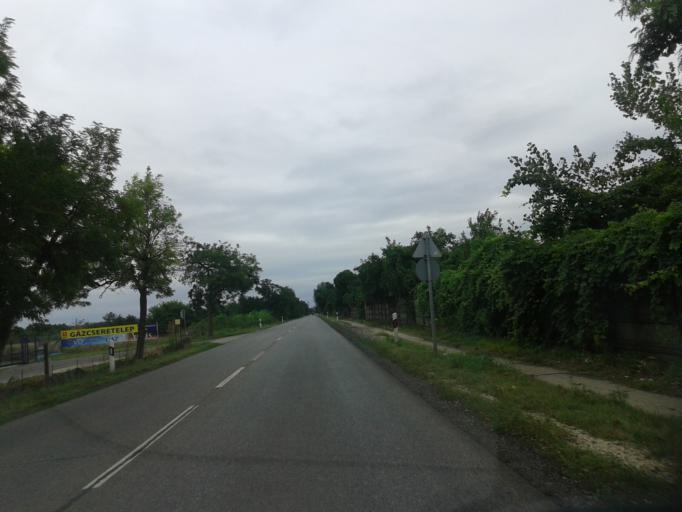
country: HU
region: Pest
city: Halasztelek
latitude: 47.3509
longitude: 18.9831
